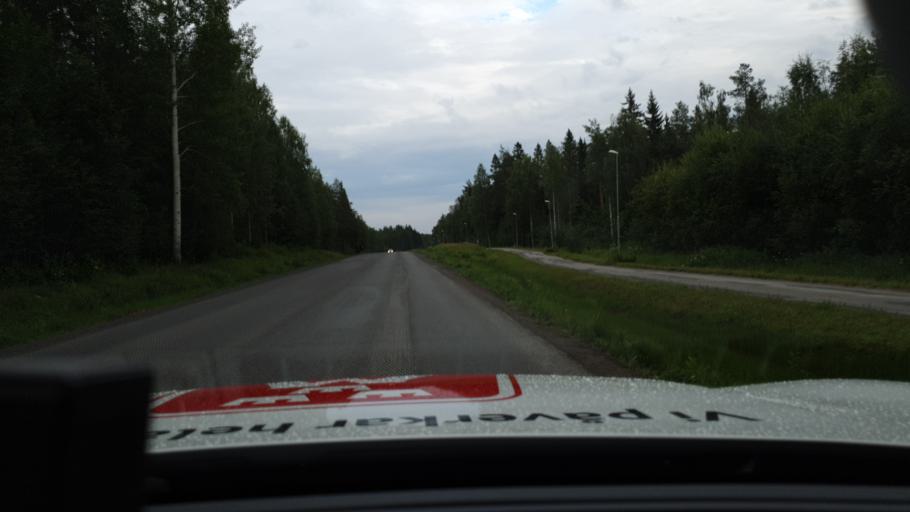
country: SE
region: Norrbotten
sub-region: Bodens Kommun
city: Boden
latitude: 65.8292
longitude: 21.6374
